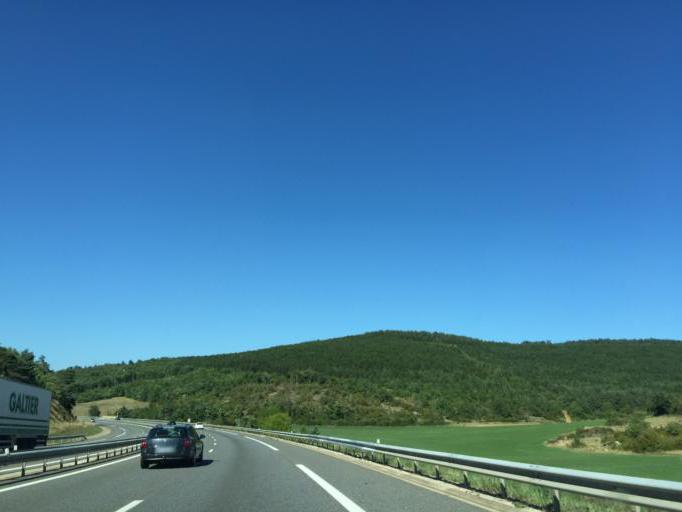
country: FR
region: Midi-Pyrenees
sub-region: Departement de l'Aveyron
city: Severac-le-Chateau
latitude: 44.3593
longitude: 3.1163
